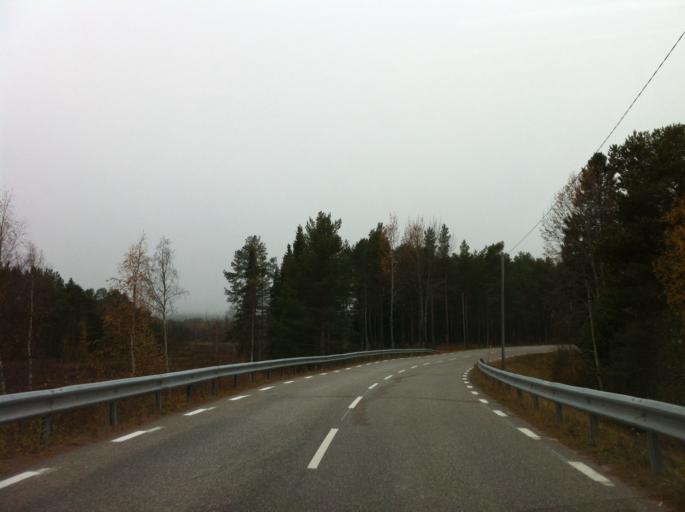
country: NO
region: Hedmark
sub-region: Trysil
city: Innbygda
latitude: 61.8566
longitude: 12.7099
